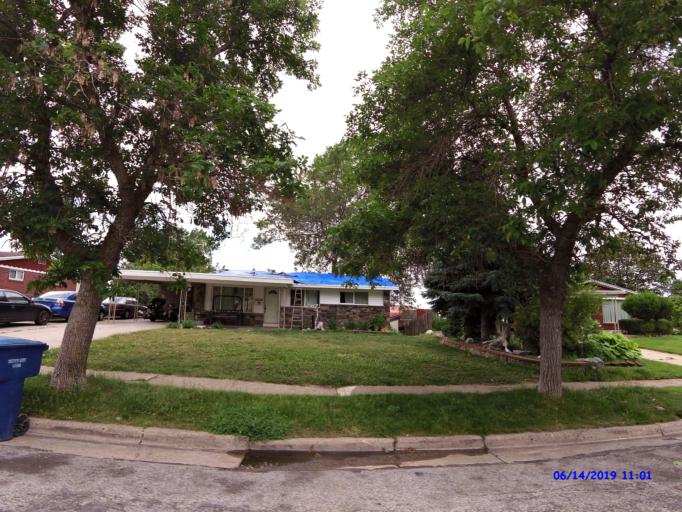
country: US
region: Utah
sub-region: Weber County
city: Ogden
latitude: 41.2465
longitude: -111.9372
